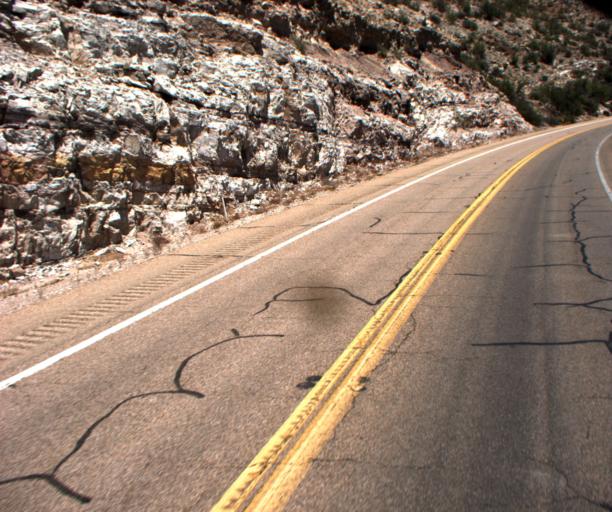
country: US
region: Arizona
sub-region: Pinal County
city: Kearny
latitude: 33.0044
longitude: -110.7648
